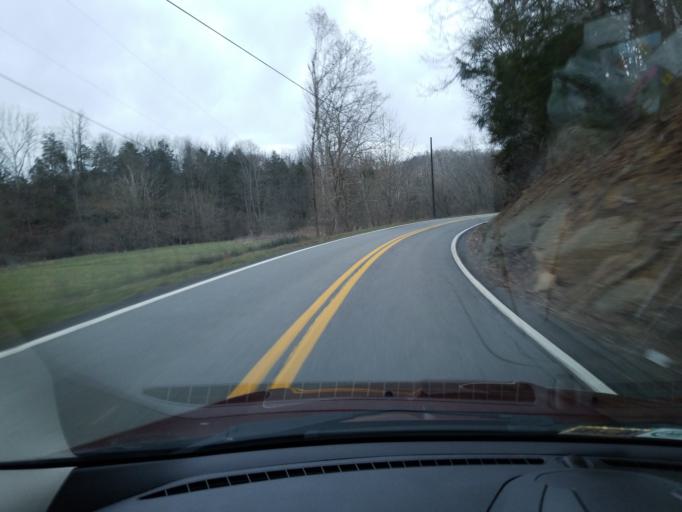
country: US
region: West Virginia
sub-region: Monroe County
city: Union
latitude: 37.5470
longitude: -80.5818
